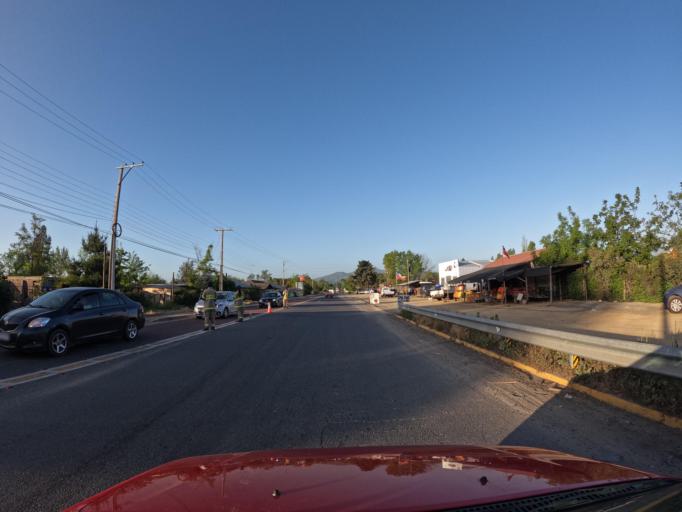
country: CL
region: O'Higgins
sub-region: Provincia de Cachapoal
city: San Vicente
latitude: -34.3115
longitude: -71.3838
